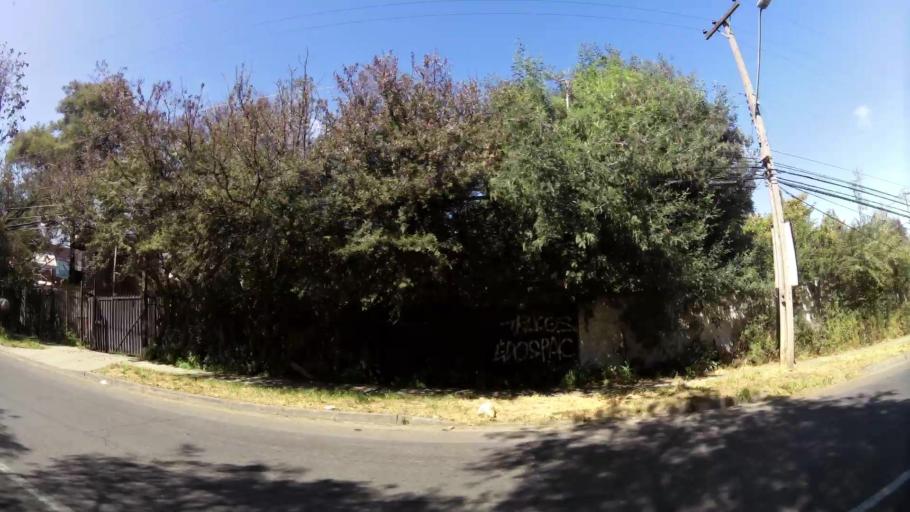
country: CL
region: Santiago Metropolitan
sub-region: Provincia de Santiago
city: Villa Presidente Frei, Nunoa, Santiago, Chile
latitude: -33.4323
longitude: -70.5290
